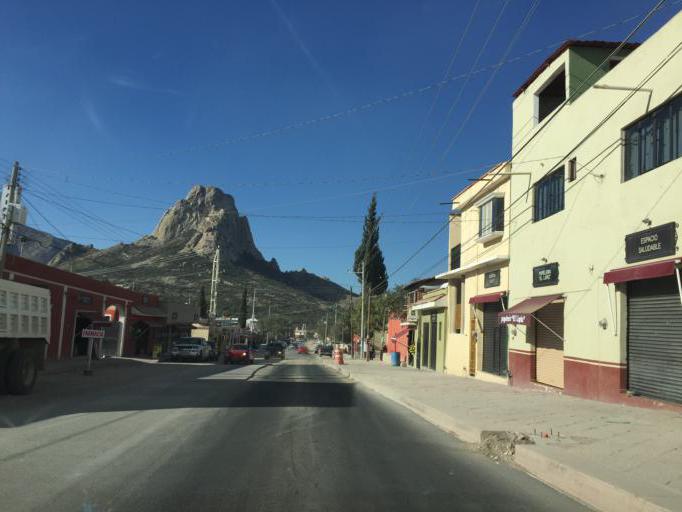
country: MX
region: Queretaro
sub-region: Ezequiel Montes
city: San Jose del Jagueey
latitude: 20.7369
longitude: -99.9378
